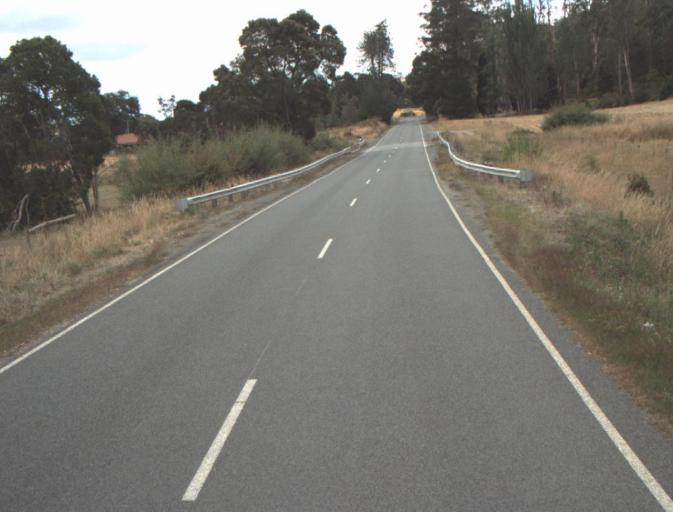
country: AU
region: Tasmania
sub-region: Launceston
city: Mayfield
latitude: -41.2328
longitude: 147.2106
